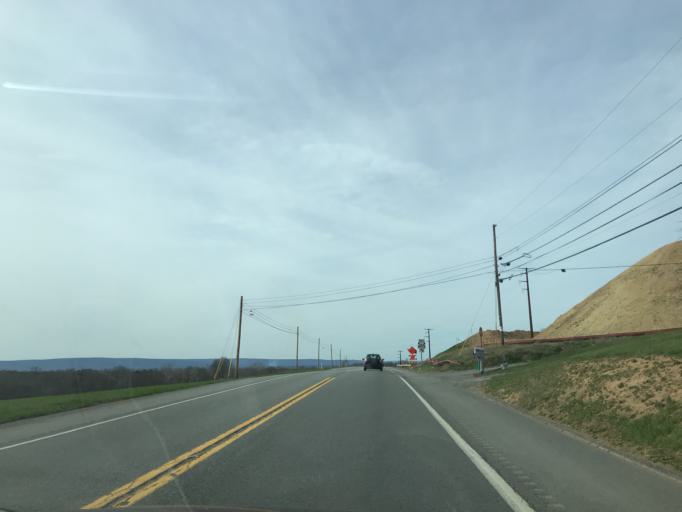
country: US
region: Pennsylvania
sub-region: Union County
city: Lewisburg
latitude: 40.9329
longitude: -76.8490
